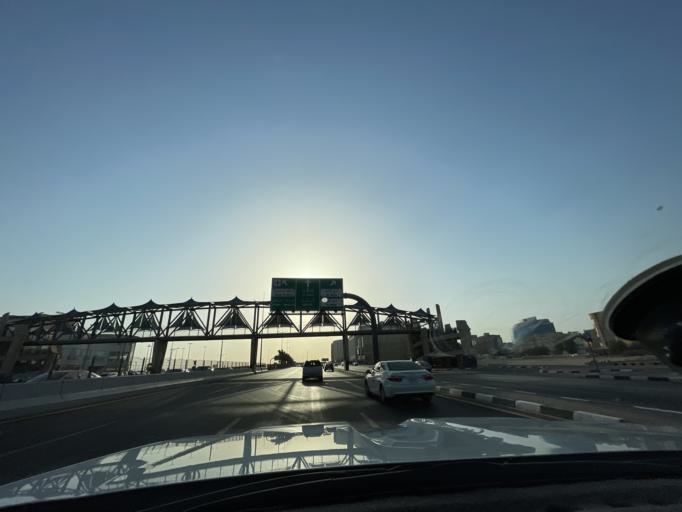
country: SA
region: Eastern Province
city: Khobar
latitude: 26.2877
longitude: 50.1851
